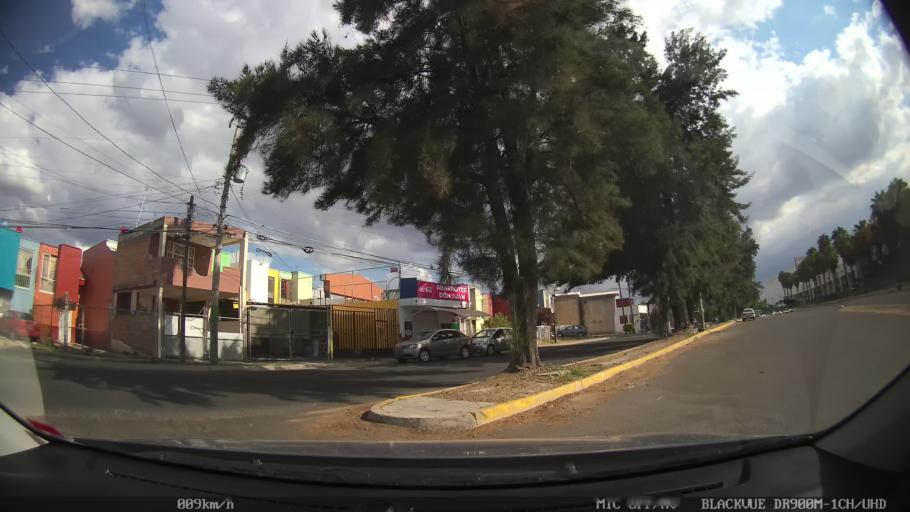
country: MX
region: Jalisco
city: Tlaquepaque
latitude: 20.6389
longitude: -103.2815
